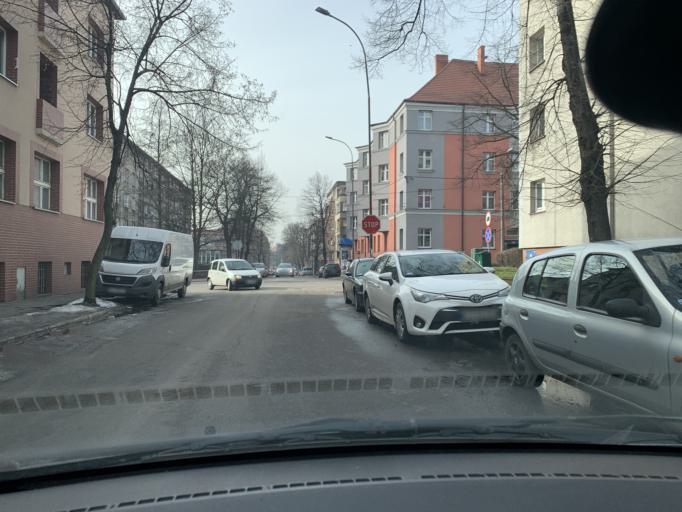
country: PL
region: Silesian Voivodeship
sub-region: Bytom
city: Bytom
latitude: 50.3555
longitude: 18.9148
